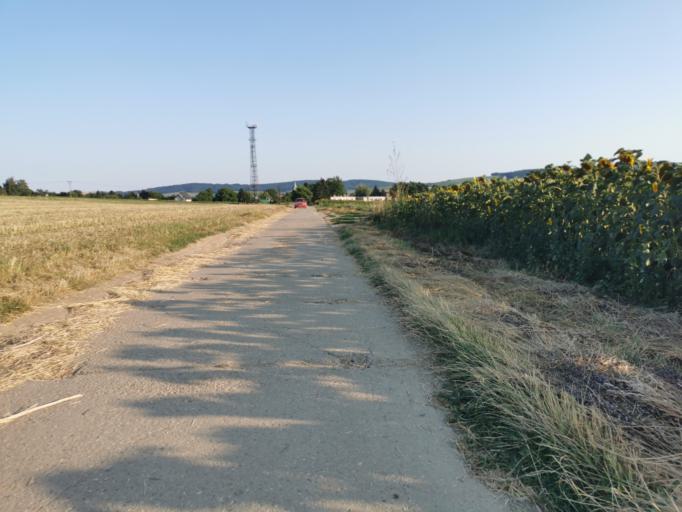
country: SK
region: Trnavsky
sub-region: Okres Skalica
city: Skalica
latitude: 48.7784
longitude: 17.2793
